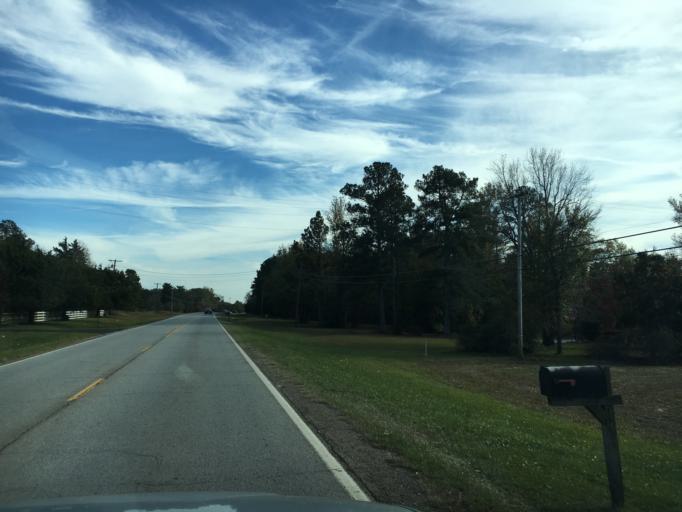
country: US
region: Georgia
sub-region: Elbert County
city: Elberton
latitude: 34.0779
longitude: -82.8393
